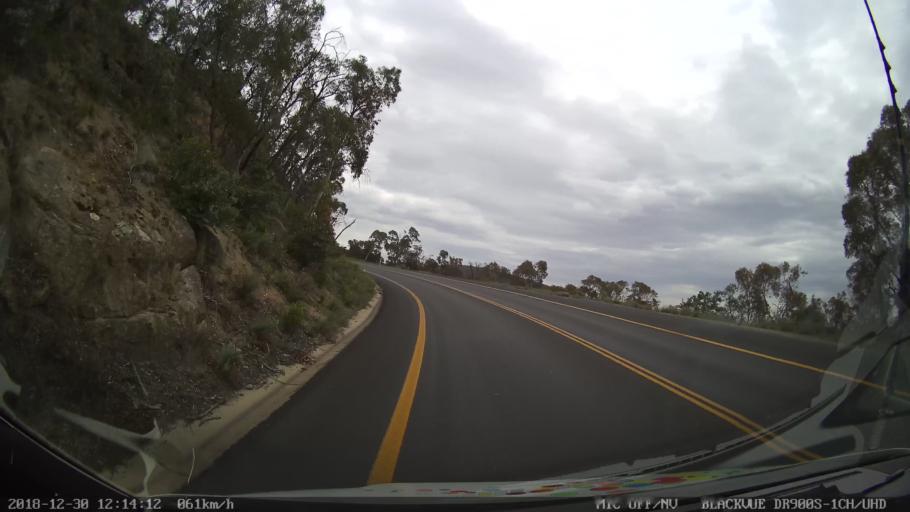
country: AU
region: New South Wales
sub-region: Snowy River
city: Jindabyne
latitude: -36.3449
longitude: 148.5813
